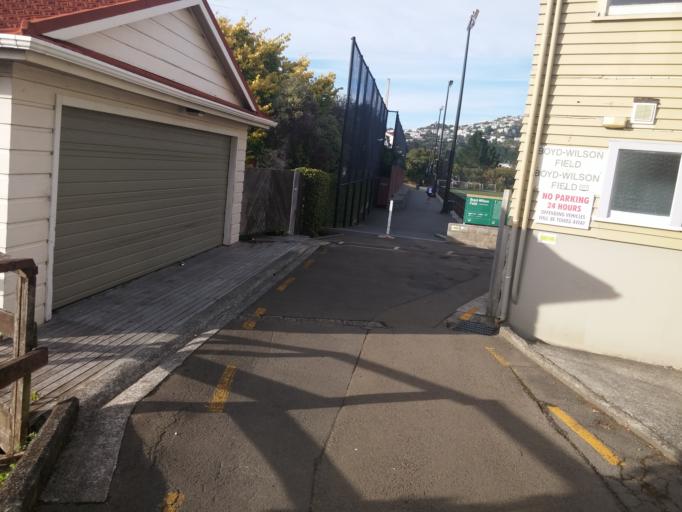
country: NZ
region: Wellington
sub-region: Wellington City
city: Wellington
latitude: -41.2918
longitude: 174.7690
